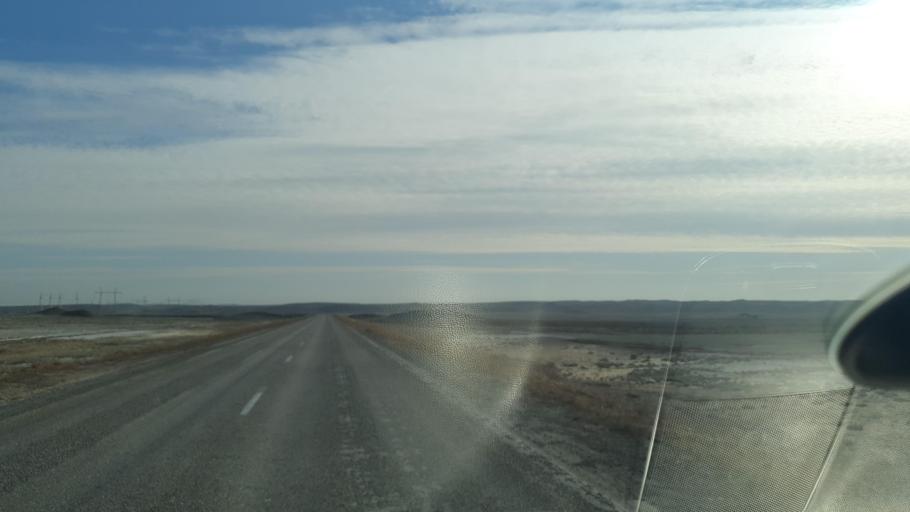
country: KZ
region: Zhambyl
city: Mynaral
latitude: 45.5703
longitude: 73.4171
